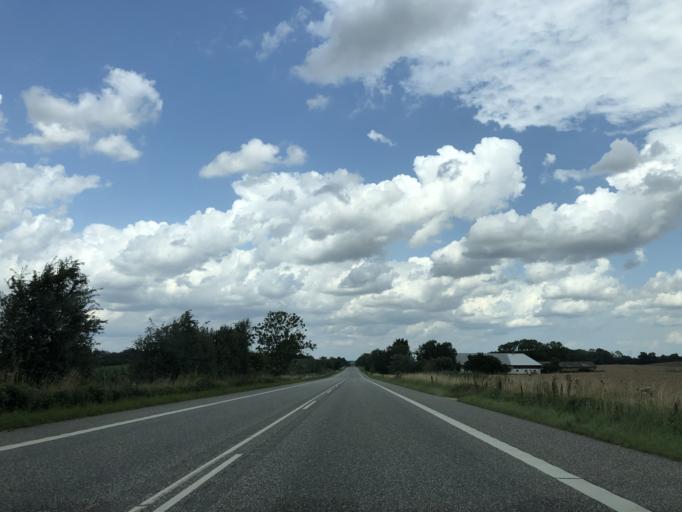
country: DK
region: South Denmark
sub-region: Aabenraa Kommune
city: Lojt Kirkeby
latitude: 55.1573
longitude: 9.4438
